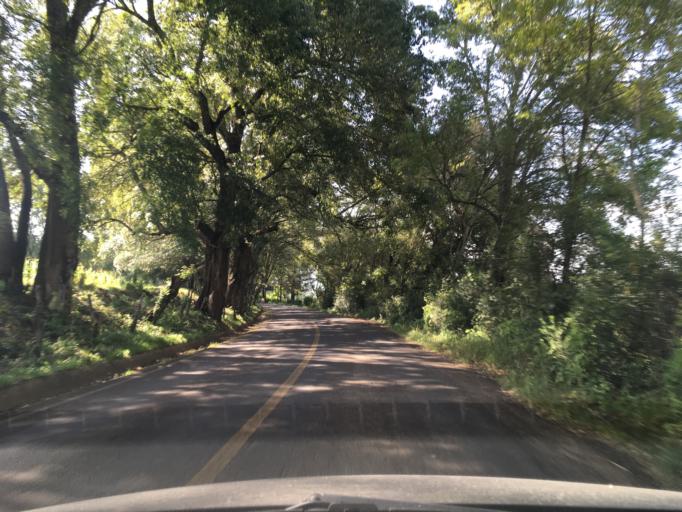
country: MX
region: Michoacan
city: Acuitzio del Canje
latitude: 19.5571
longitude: -101.2710
